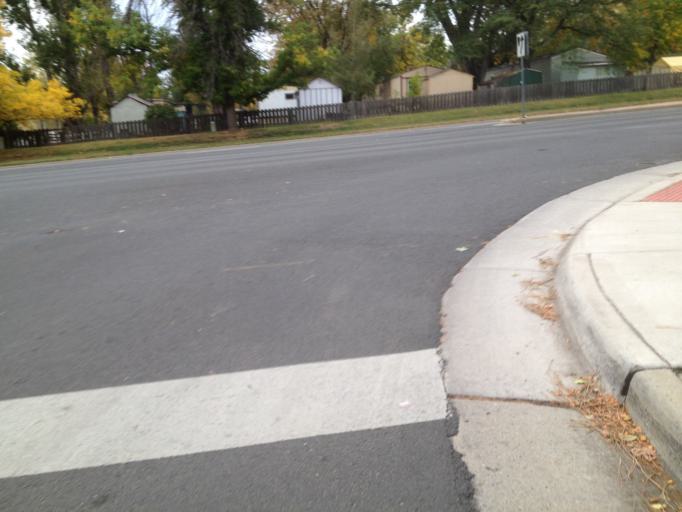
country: US
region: Colorado
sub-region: Boulder County
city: Louisville
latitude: 39.9872
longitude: -105.1445
